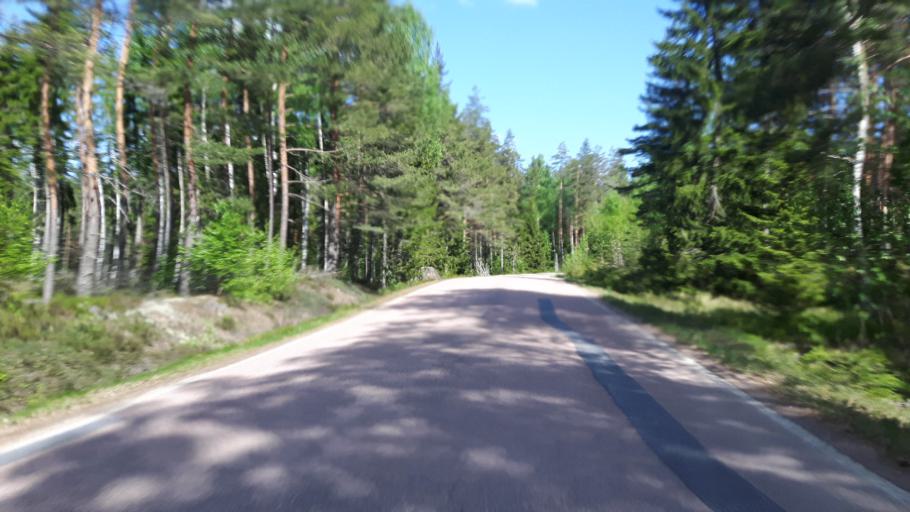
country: FI
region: Kymenlaakso
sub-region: Kotka-Hamina
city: Virolahti
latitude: 60.5489
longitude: 27.6565
